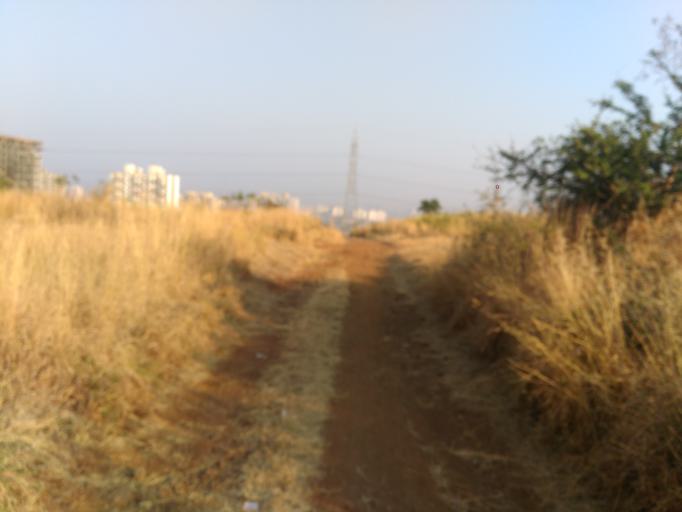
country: IN
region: Maharashtra
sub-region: Pune Division
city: Pune
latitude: 18.4302
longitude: 73.9016
